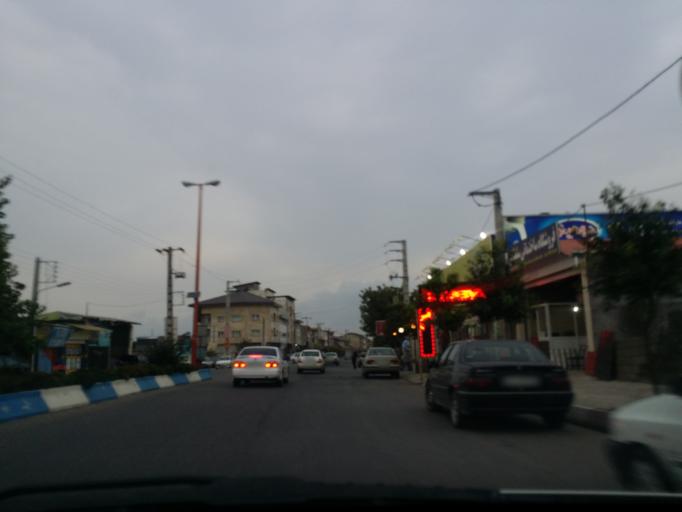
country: IR
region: Mazandaran
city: `Abbasabad
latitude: 36.7216
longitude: 51.1031
